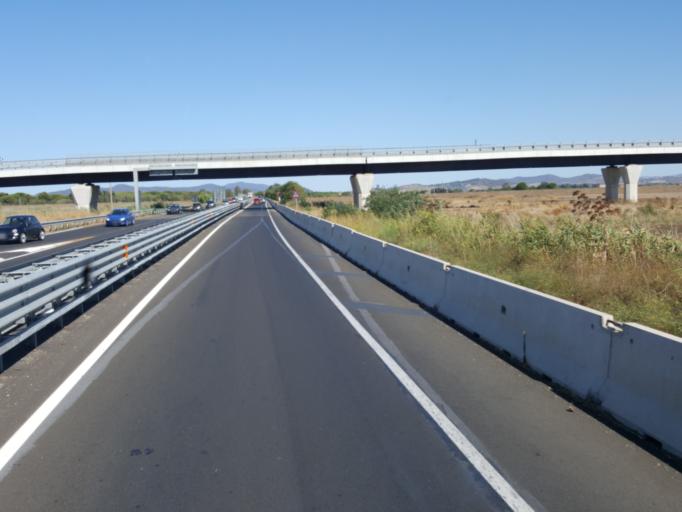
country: IT
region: Tuscany
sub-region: Provincia di Grosseto
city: Albinia
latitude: 42.5033
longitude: 11.2017
